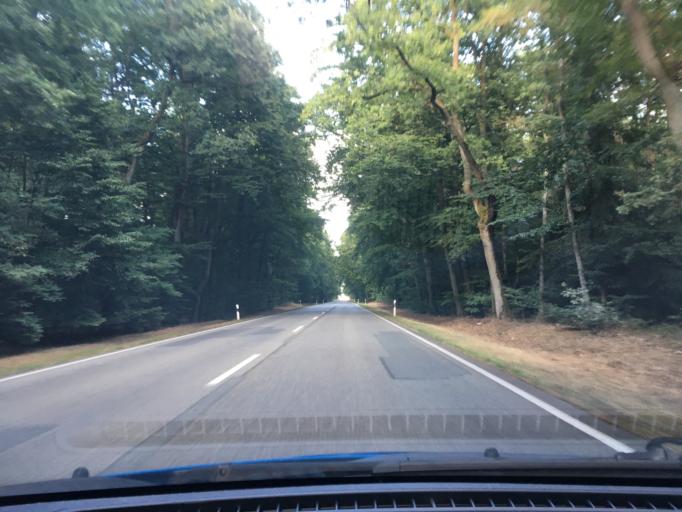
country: DE
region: Mecklenburg-Vorpommern
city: Gross Laasch
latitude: 53.3691
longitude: 11.5593
